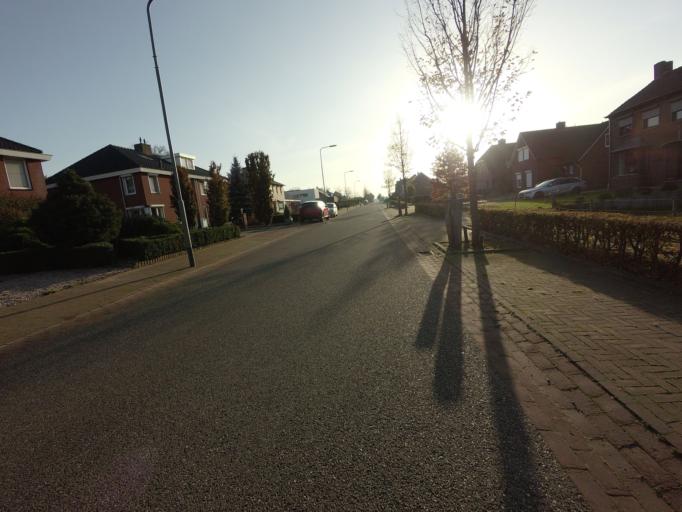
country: DE
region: North Rhine-Westphalia
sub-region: Regierungsbezirk Koln
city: Waldfeucht
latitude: 51.0813
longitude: 5.9648
